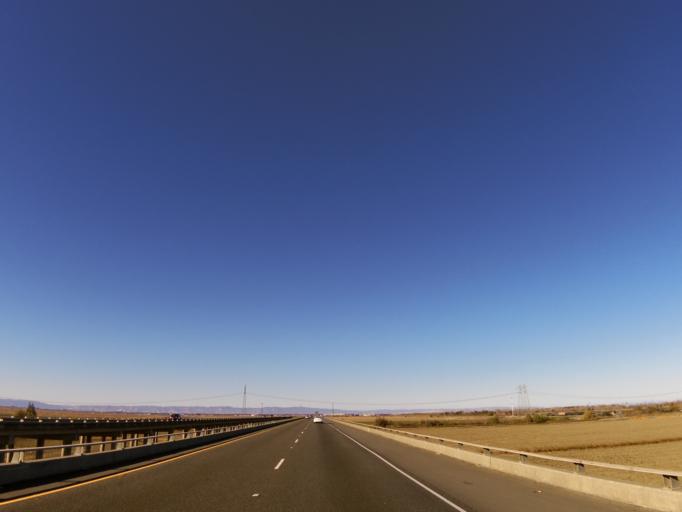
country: US
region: California
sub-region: Yolo County
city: Woodland
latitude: 38.6736
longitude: -121.6667
